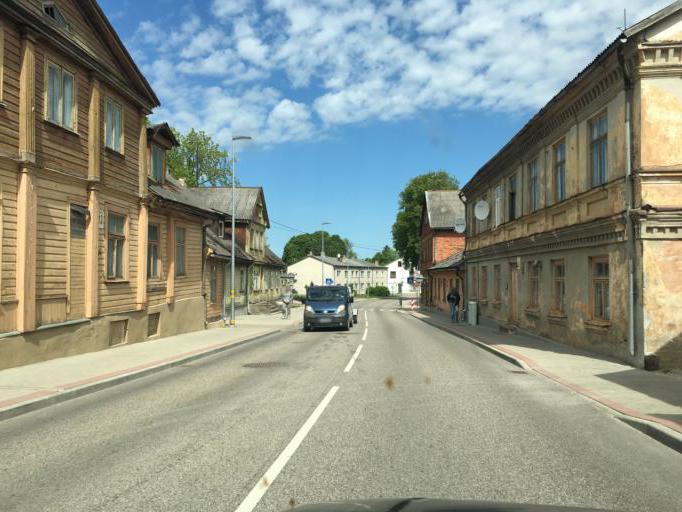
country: LV
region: Talsu Rajons
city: Valdemarpils
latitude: 57.3720
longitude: 22.5914
